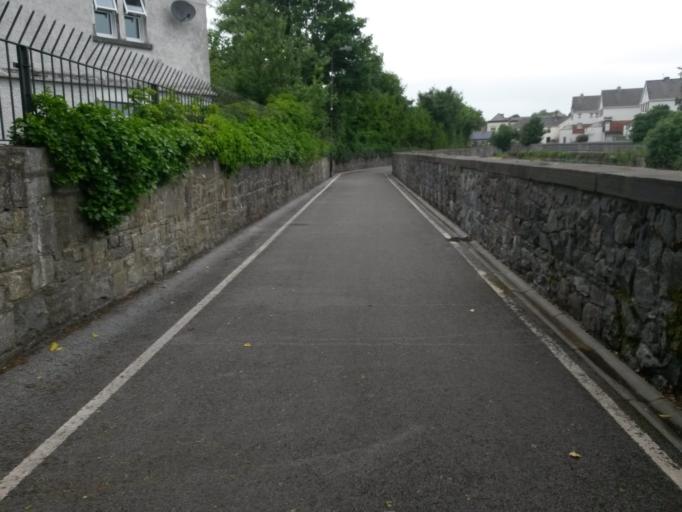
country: IE
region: Munster
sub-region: An Clar
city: Ennis
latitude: 52.8449
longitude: -8.9882
